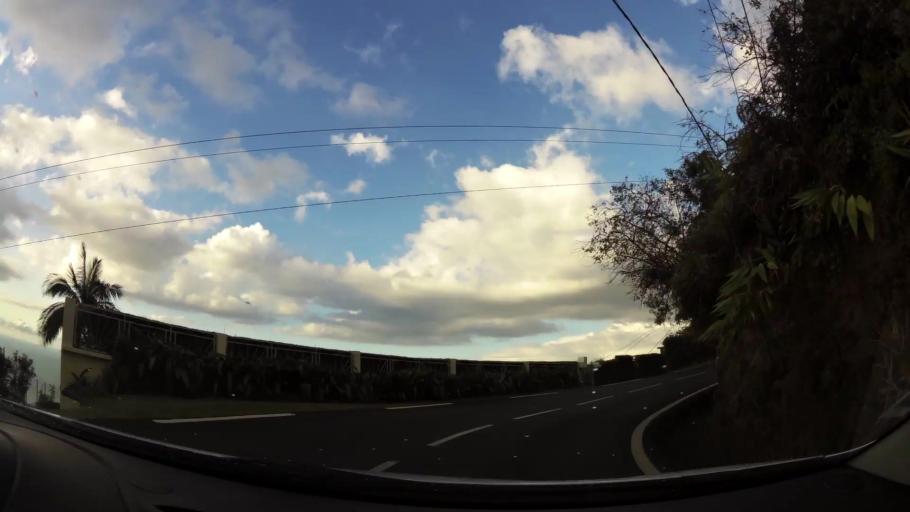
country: RE
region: Reunion
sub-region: Reunion
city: Saint-Denis
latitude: -20.9103
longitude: 55.4414
